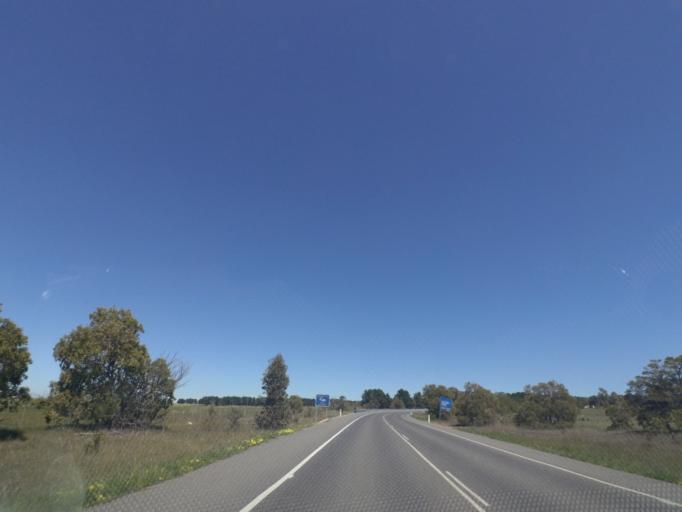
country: AU
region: Victoria
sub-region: Hume
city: Sunbury
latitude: -37.3097
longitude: 144.8531
